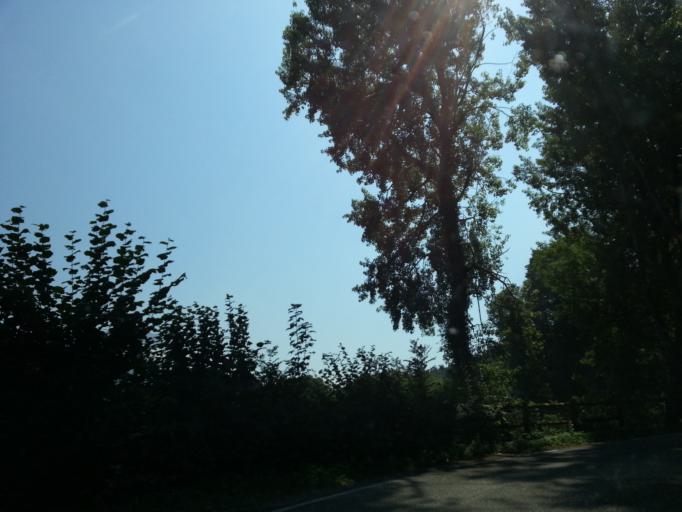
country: FR
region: Rhone-Alpes
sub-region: Departement de la Haute-Savoie
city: Villaz
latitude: 45.9162
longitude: 6.1800
